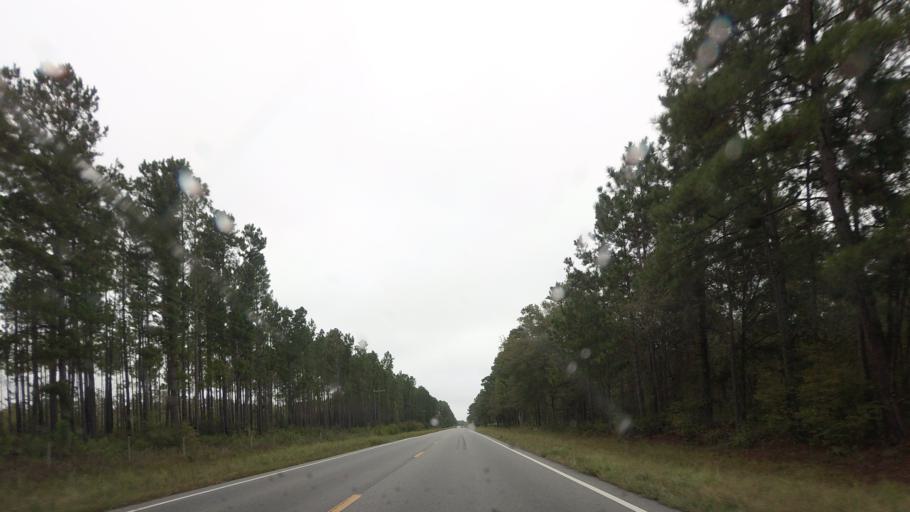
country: US
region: Georgia
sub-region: Berrien County
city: Nashville
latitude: 31.2679
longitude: -83.2397
